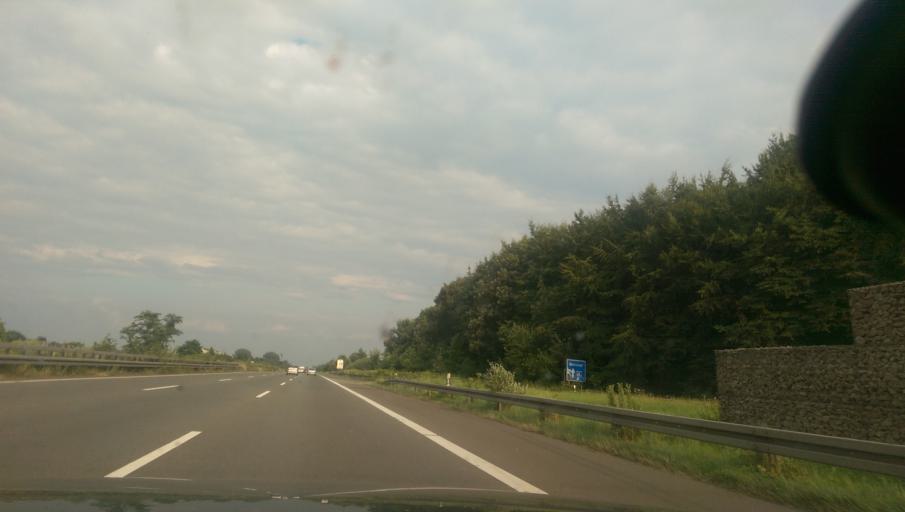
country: DE
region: North Rhine-Westphalia
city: Waltrop
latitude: 51.5820
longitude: 7.4339
